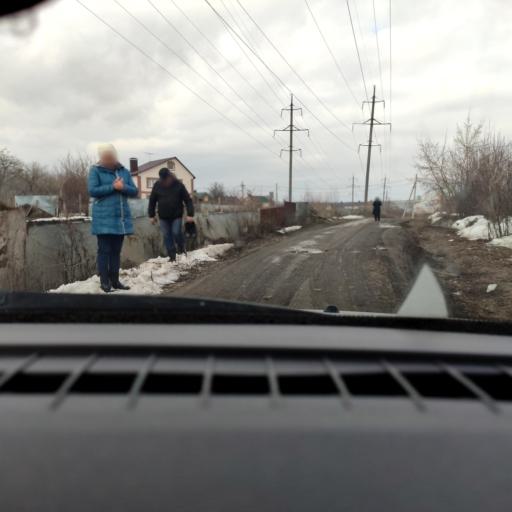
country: RU
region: Samara
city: Petra-Dubrava
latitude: 53.2891
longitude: 50.3117
